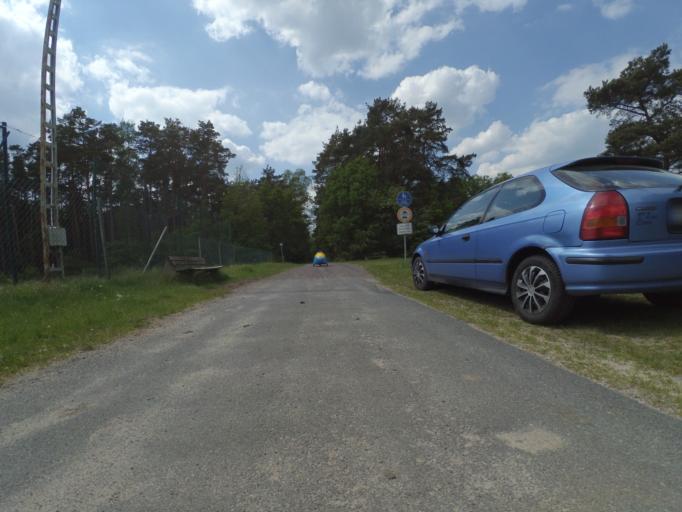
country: DE
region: Lower Saxony
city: Winsen (Aller)
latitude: 52.6733
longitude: 9.8955
